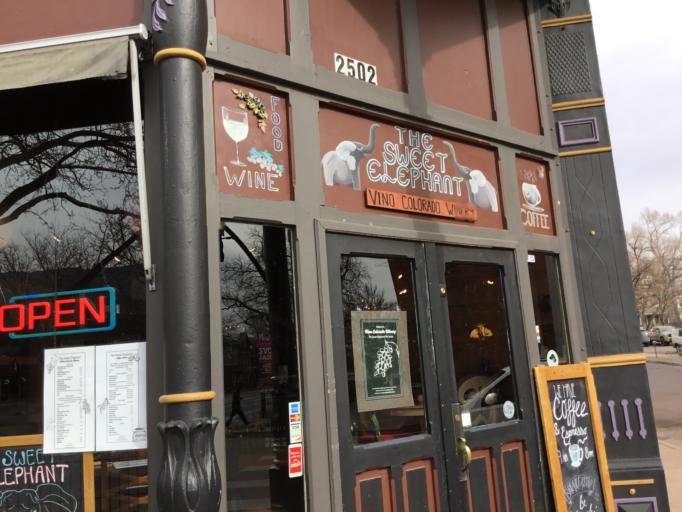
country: US
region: Colorado
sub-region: El Paso County
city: Colorado Springs
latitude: 38.8474
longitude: -104.8627
